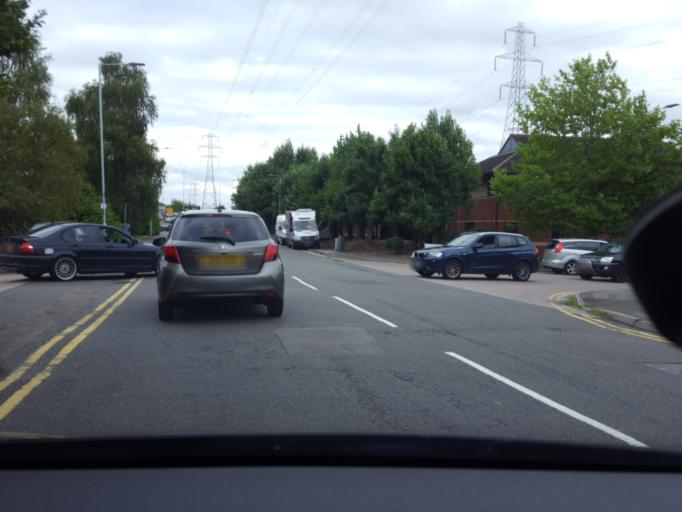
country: GB
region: England
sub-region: Leicestershire
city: Enderby
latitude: 52.6020
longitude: -1.1904
